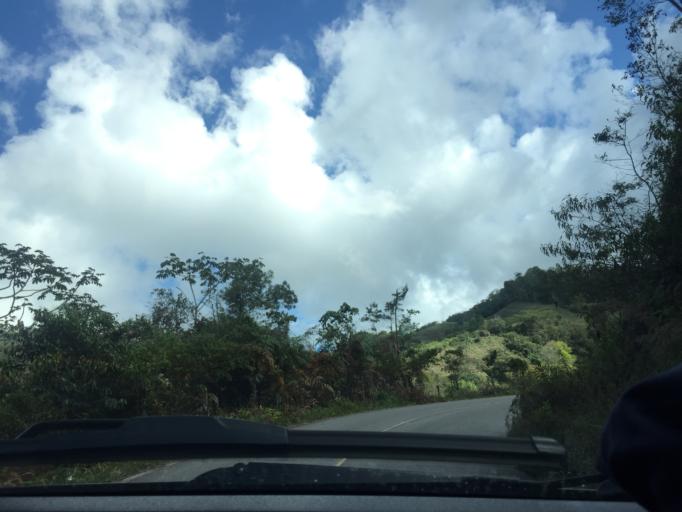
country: CO
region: Cundinamarca
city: San Francisco
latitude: 5.0185
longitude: -74.2769
